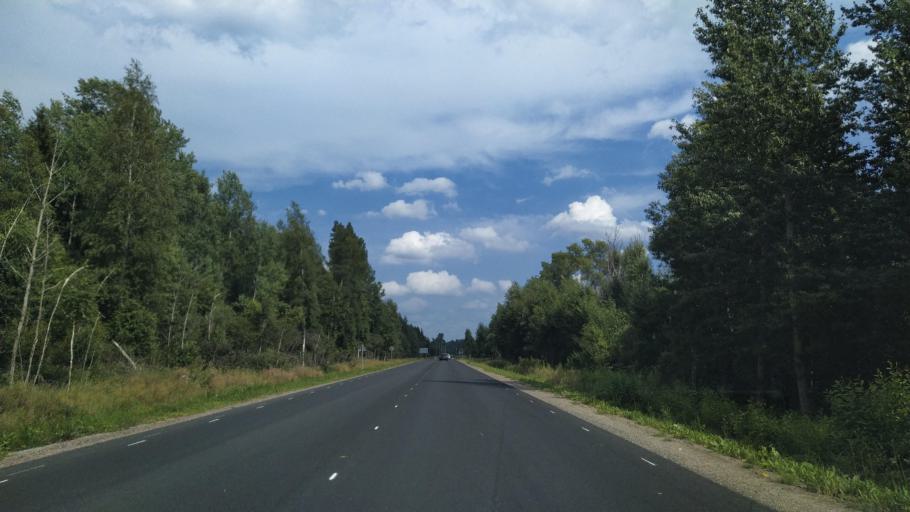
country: RU
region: Pskov
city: Vybor
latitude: 57.7080
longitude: 28.8948
